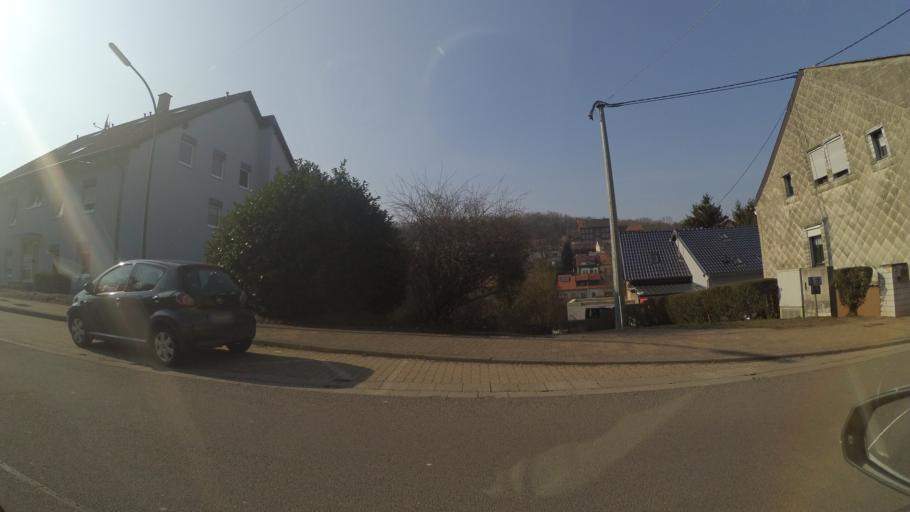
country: DE
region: Saarland
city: Sulzbach
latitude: 49.3056
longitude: 7.0792
